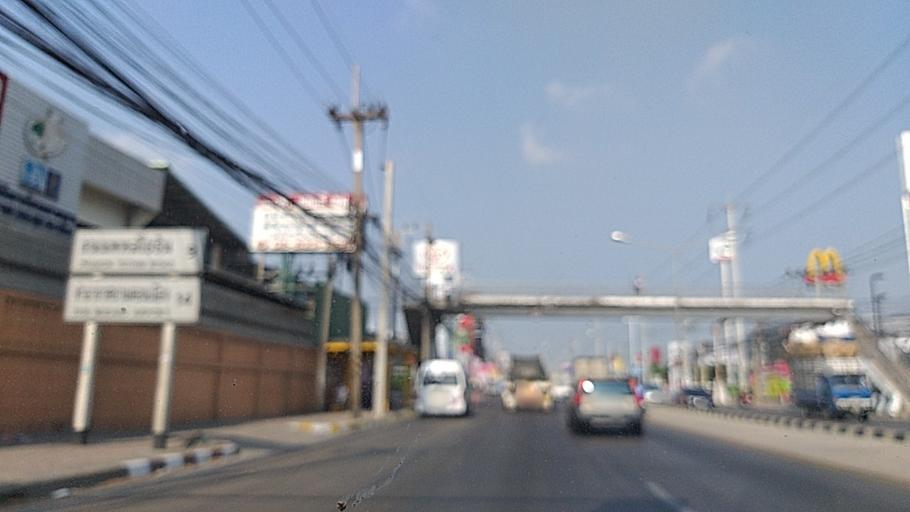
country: TH
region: Bangkok
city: Sai Mai
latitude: 13.9326
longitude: 100.6825
